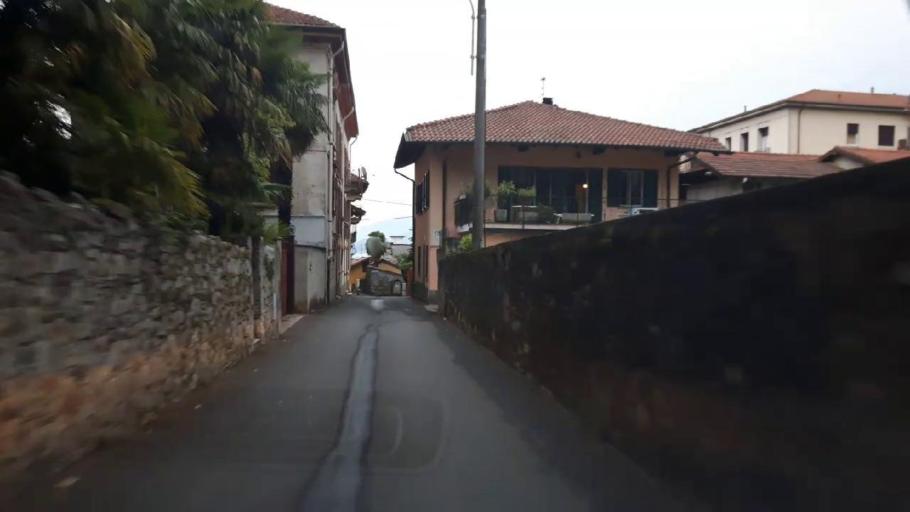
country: IT
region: Piedmont
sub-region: Provincia Verbano-Cusio-Ossola
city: Baveno
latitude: 45.9094
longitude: 8.5034
